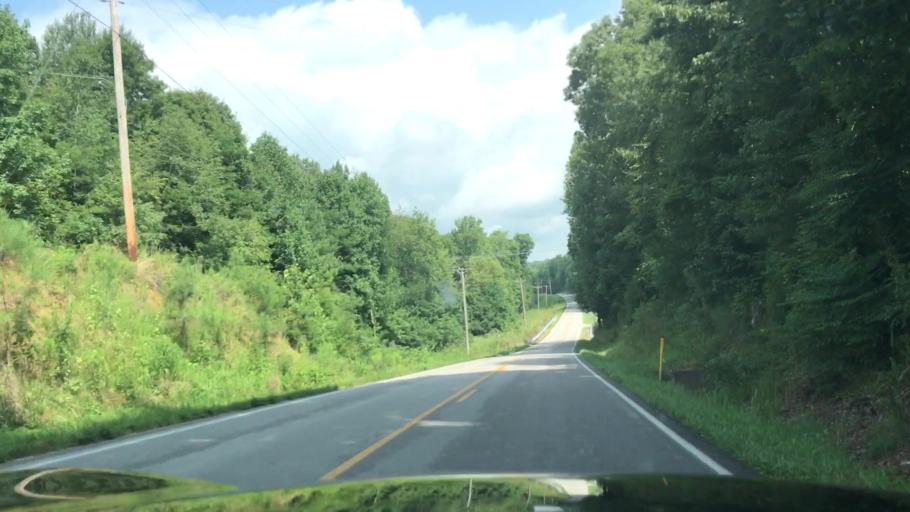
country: US
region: Kentucky
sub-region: Ohio County
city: Oak Grove
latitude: 37.1923
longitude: -86.8831
